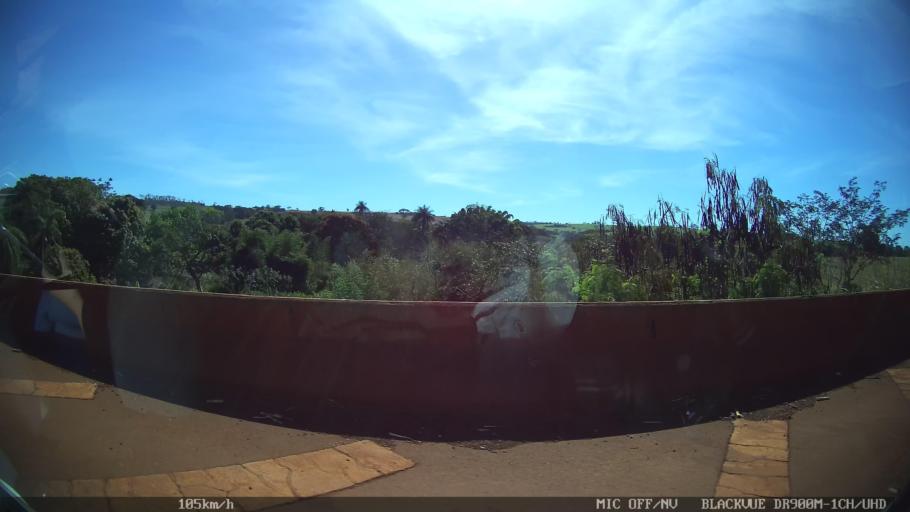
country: BR
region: Sao Paulo
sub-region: Sao Joaquim Da Barra
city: Sao Joaquim da Barra
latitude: -20.5523
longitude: -47.6608
